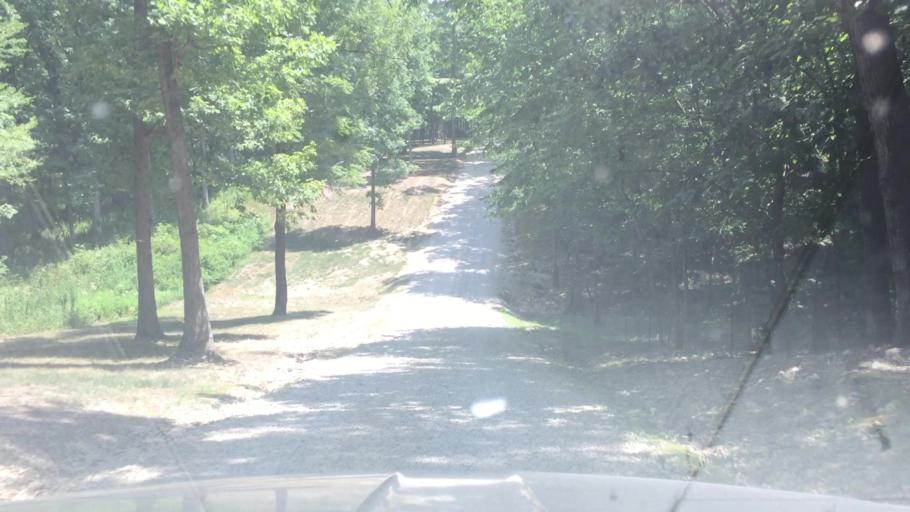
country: US
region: Missouri
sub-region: Miller County
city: Tuscumbia
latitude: 38.1310
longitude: -92.4431
